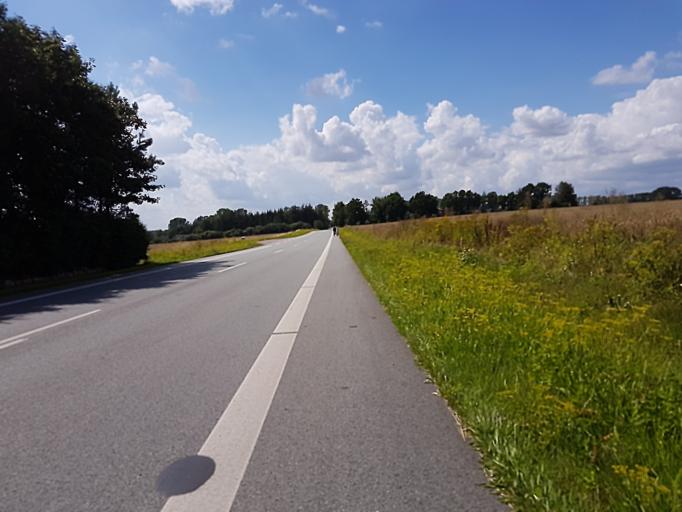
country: DK
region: Capital Region
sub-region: Egedal Kommune
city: Ganlose
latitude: 55.7853
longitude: 12.2953
